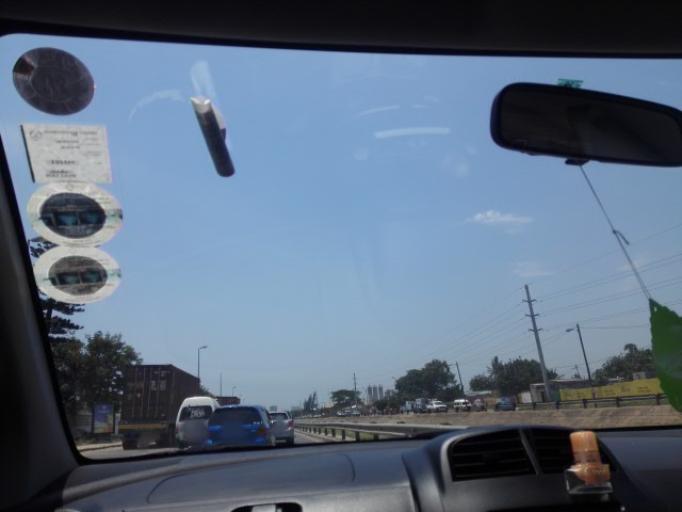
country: MZ
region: Maputo City
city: Maputo
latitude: -25.9382
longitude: 32.5672
